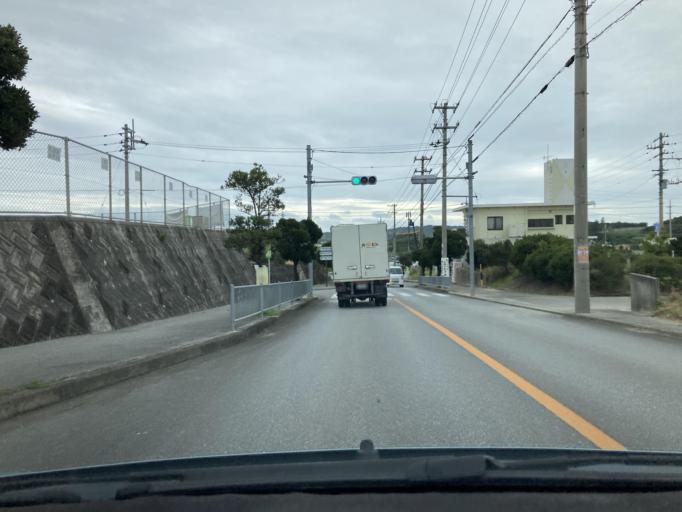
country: JP
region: Okinawa
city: Tomigusuku
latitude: 26.1619
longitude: 127.7083
